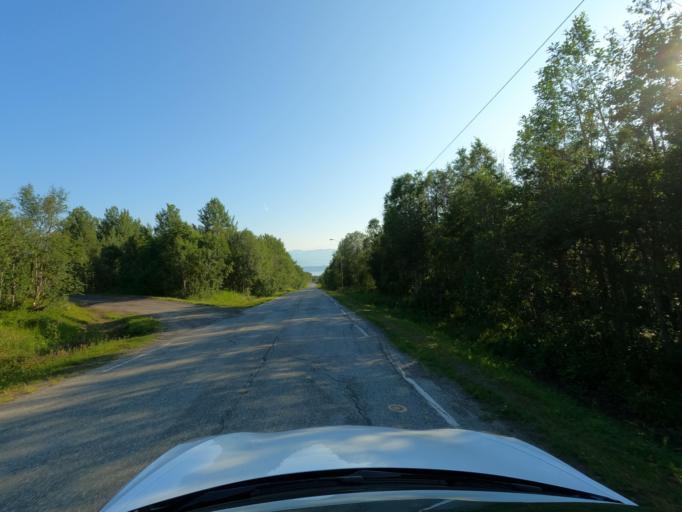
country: NO
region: Nordland
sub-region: Narvik
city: Bjerkvik
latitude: 68.5395
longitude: 17.4887
